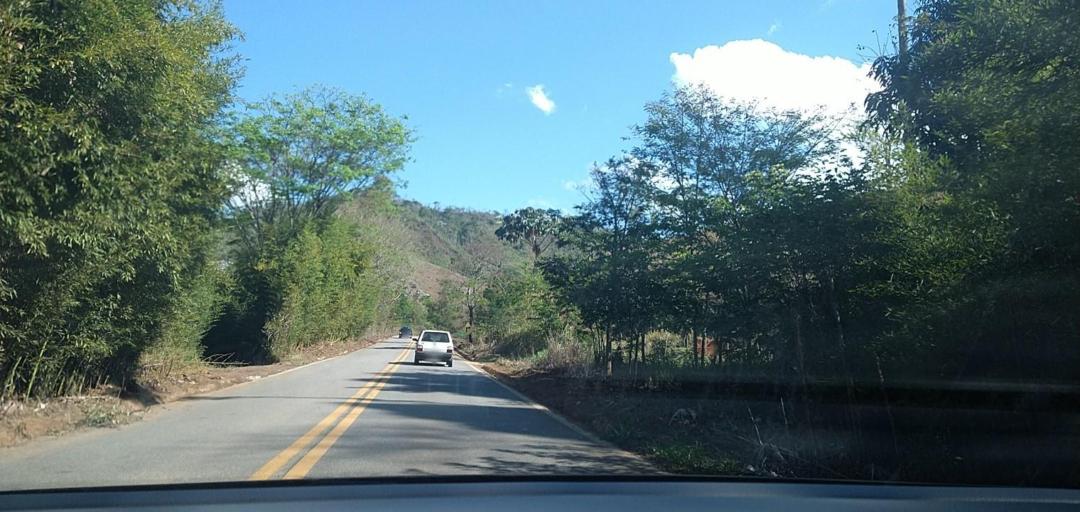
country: BR
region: Minas Gerais
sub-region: Alvinopolis
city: Alvinopolis
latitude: -20.0401
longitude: -43.0322
